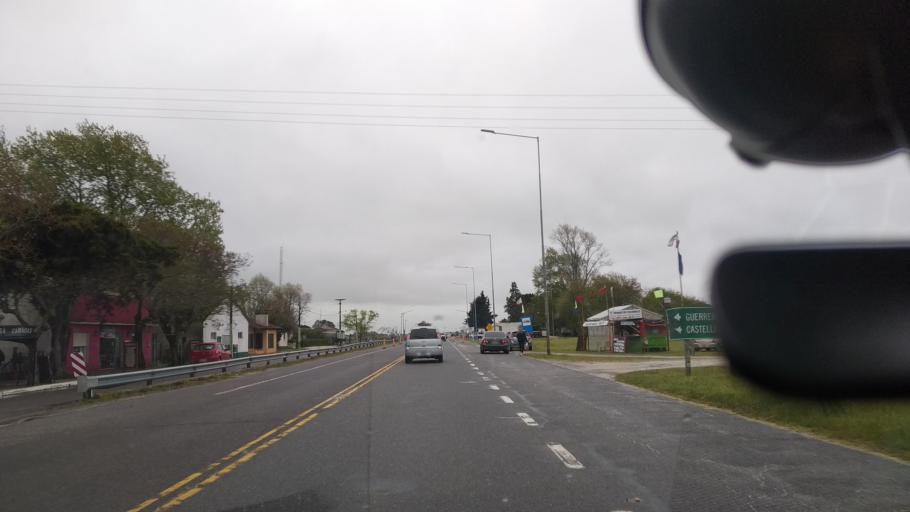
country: AR
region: Buenos Aires
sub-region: Partido de Castelli
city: Castelli
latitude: -35.9750
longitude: -57.4496
